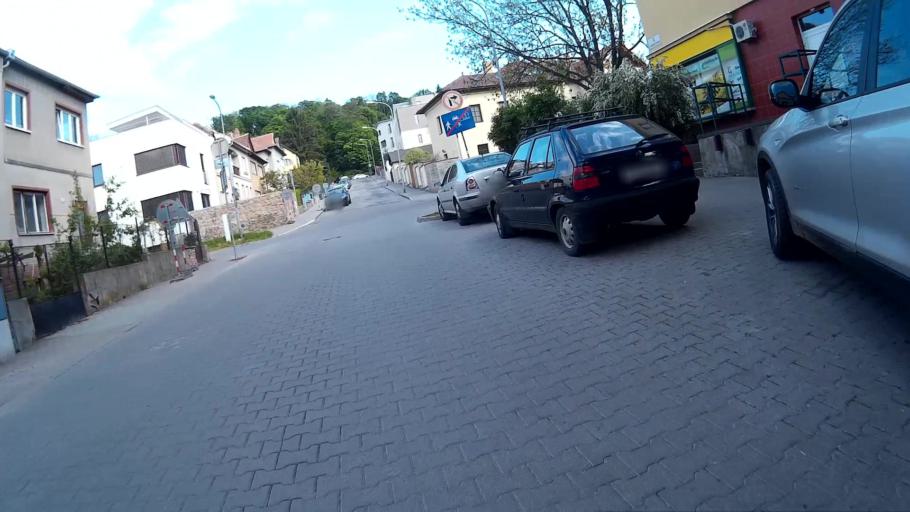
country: CZ
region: South Moravian
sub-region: Mesto Brno
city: Brno
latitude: 49.2105
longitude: 16.5767
